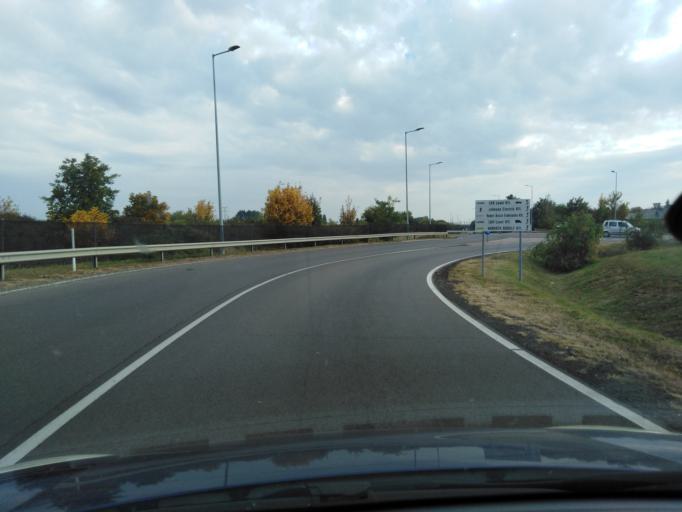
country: HU
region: Heves
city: Hatvan
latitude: 47.6778
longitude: 19.6687
